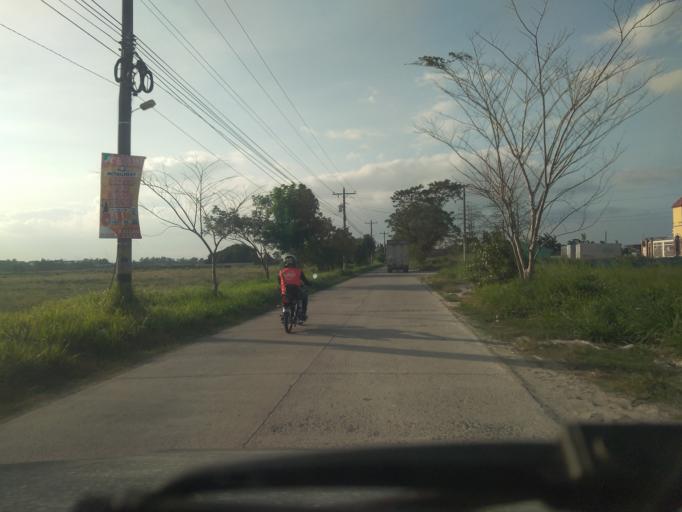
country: PH
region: Central Luzon
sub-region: Province of Pampanga
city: Malino
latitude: 15.1068
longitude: 120.6714
